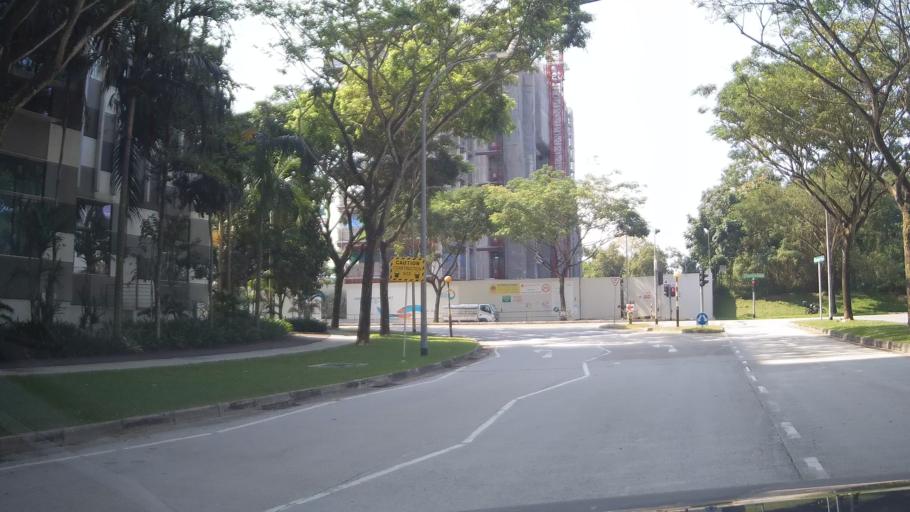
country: MY
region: Johor
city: Johor Bahru
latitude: 1.3554
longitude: 103.6930
